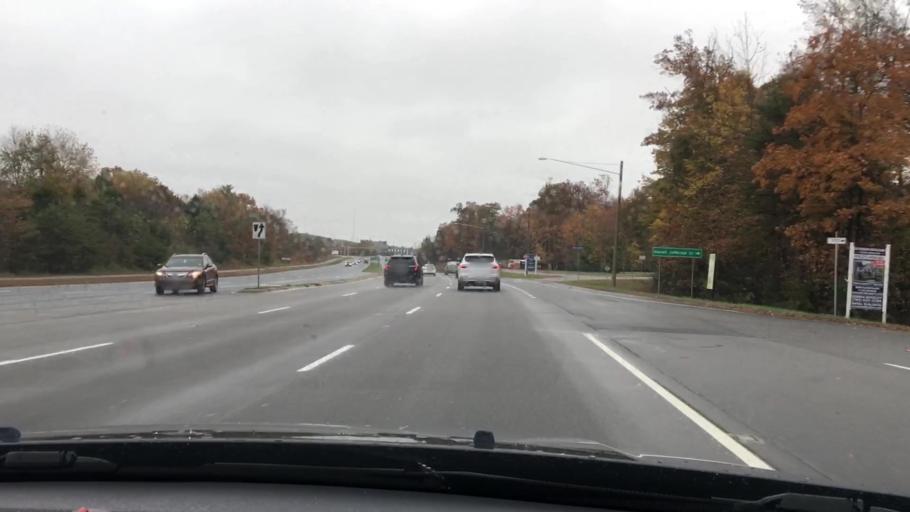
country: US
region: Virginia
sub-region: Fairfax County
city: Lorton
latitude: 38.7041
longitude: -77.2595
